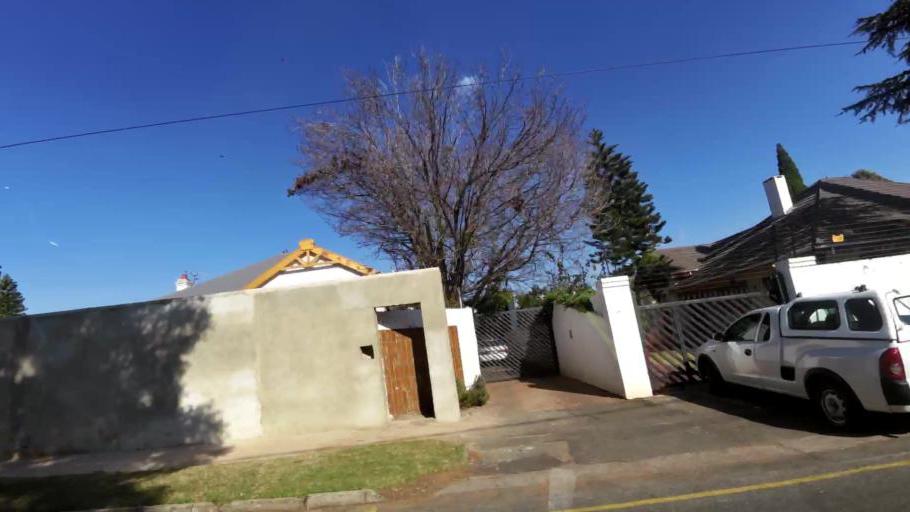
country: ZA
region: Gauteng
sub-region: City of Johannesburg Metropolitan Municipality
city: Johannesburg
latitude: -26.1768
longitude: 28.0054
